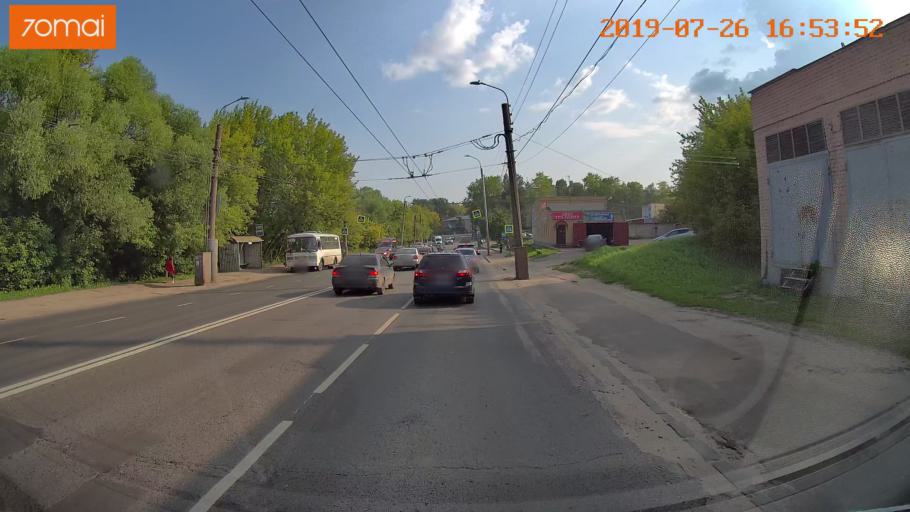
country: RU
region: Ivanovo
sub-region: Gorod Ivanovo
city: Ivanovo
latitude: 57.0123
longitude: 41.0008
